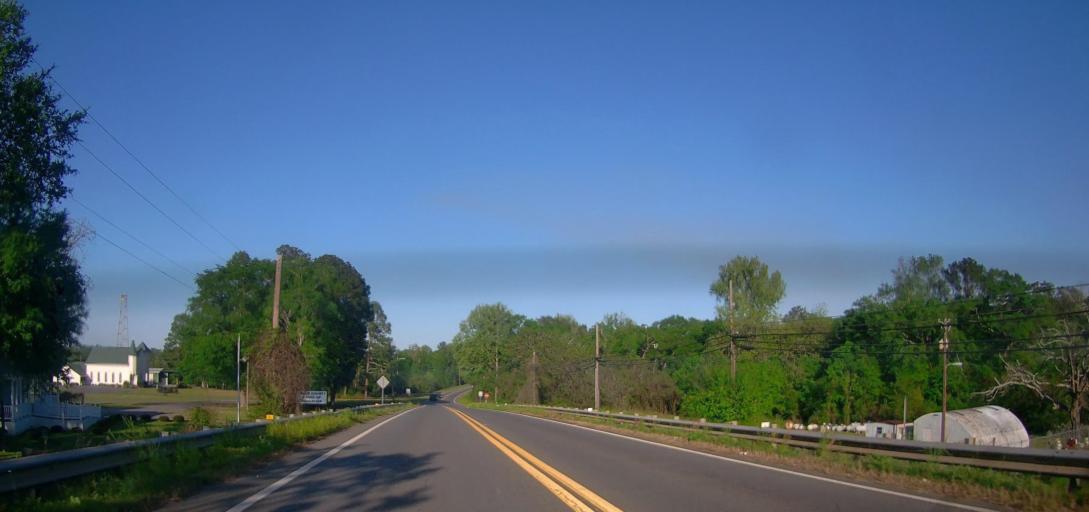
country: US
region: Georgia
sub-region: Macon County
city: Oglethorpe
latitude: 32.2957
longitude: -84.0565
